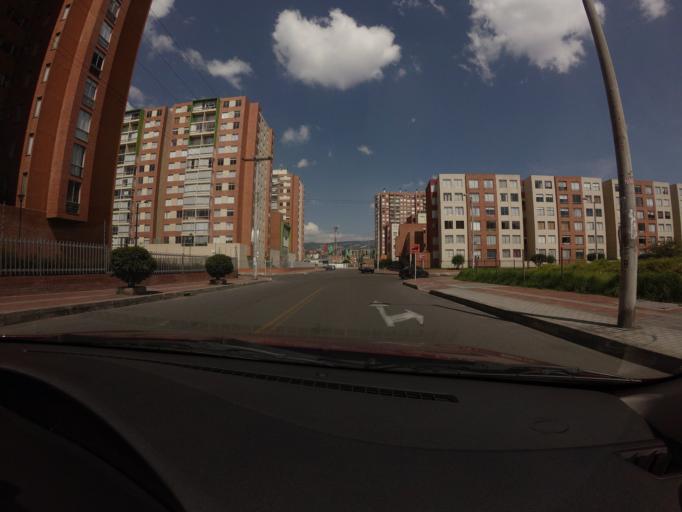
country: CO
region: Cundinamarca
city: Cota
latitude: 4.7433
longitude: -74.0620
